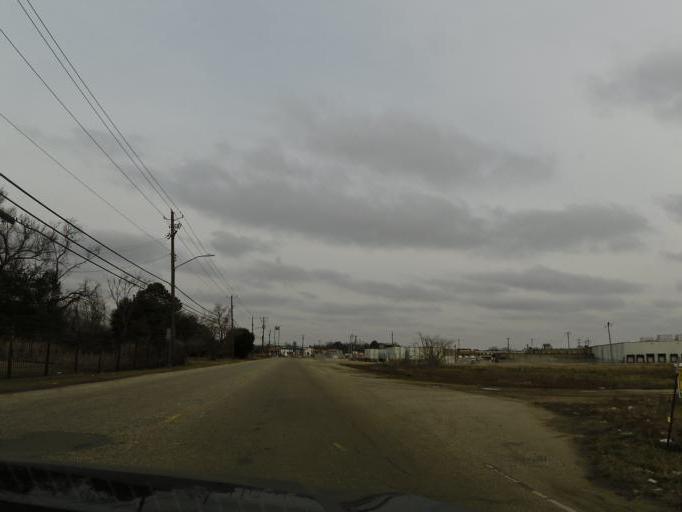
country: US
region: Alabama
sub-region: Montgomery County
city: Montgomery
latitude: 32.4006
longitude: -86.3083
